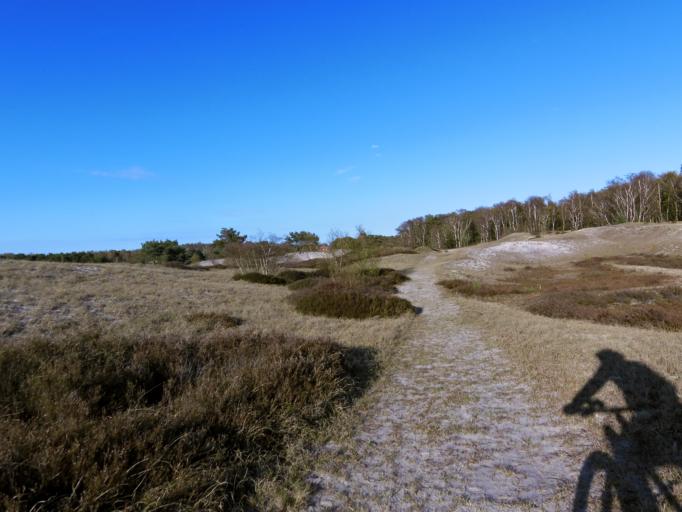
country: DE
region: Mecklenburg-Vorpommern
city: Hiddensee
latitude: 54.5413
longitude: 13.0977
